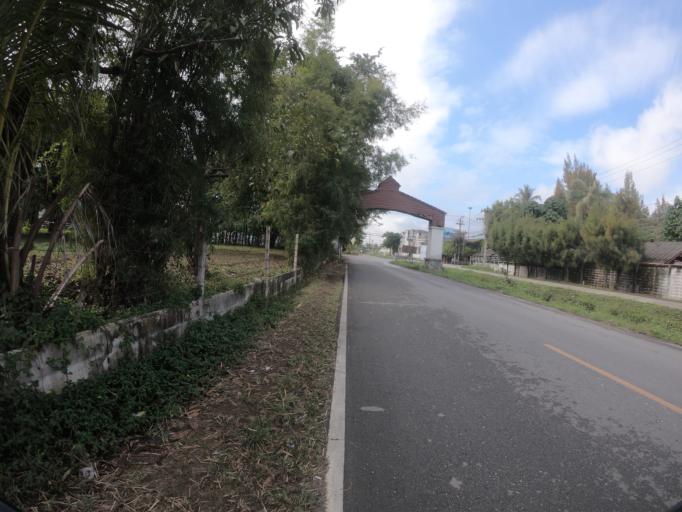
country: TH
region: Chiang Mai
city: Hang Dong
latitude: 18.7271
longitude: 98.9498
